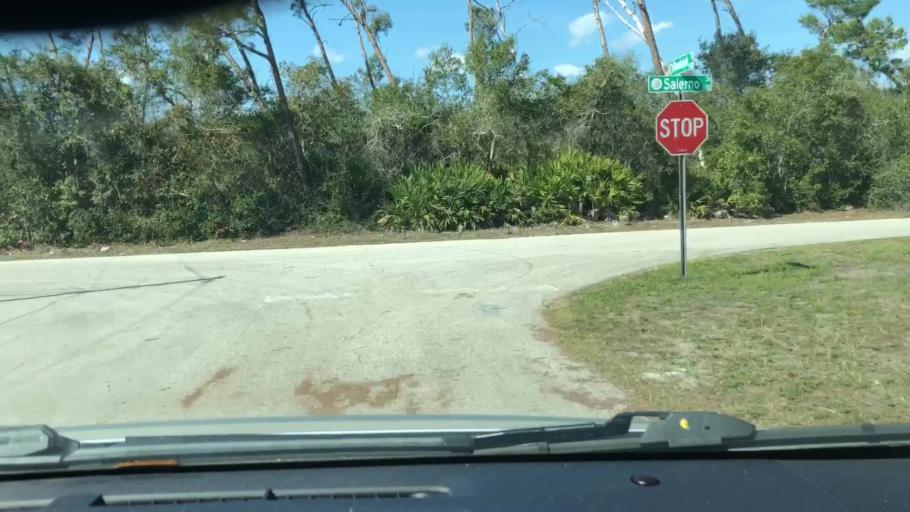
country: US
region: Florida
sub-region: Volusia County
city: Deltona
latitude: 28.8805
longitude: -81.2366
